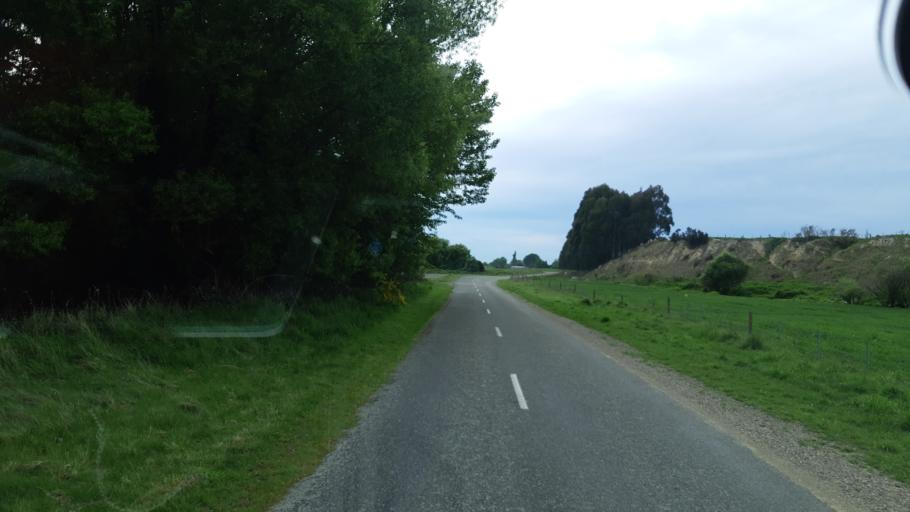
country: NZ
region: Canterbury
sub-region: Timaru District
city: Timaru
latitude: -44.5408
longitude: 171.1416
